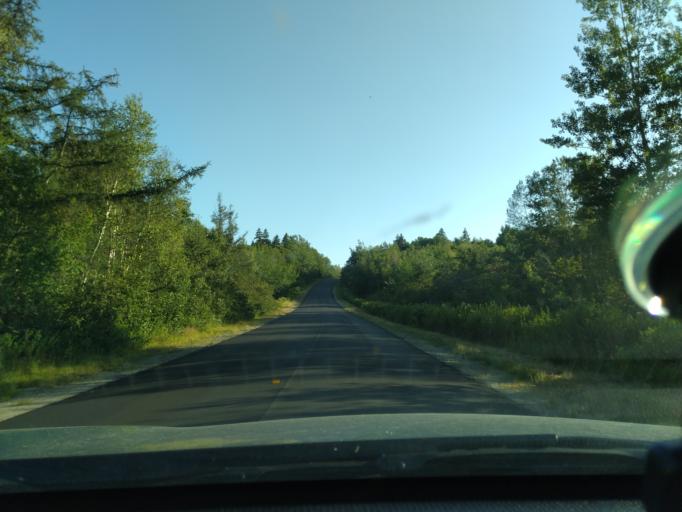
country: US
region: Maine
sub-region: Washington County
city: Eastport
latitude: 44.7163
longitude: -67.1374
